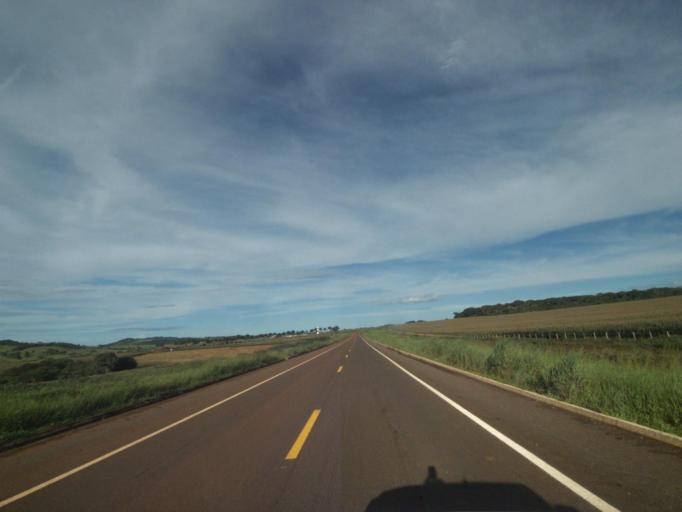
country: BR
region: Goias
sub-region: Jaragua
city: Jaragua
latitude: -15.9037
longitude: -49.5435
